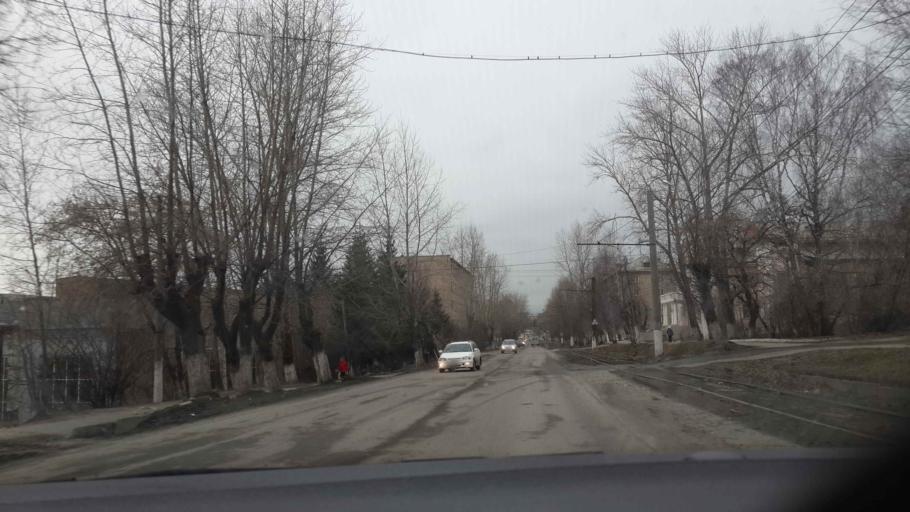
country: RU
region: Chelyabinsk
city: Zlatoust
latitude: 55.2013
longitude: 59.7234
